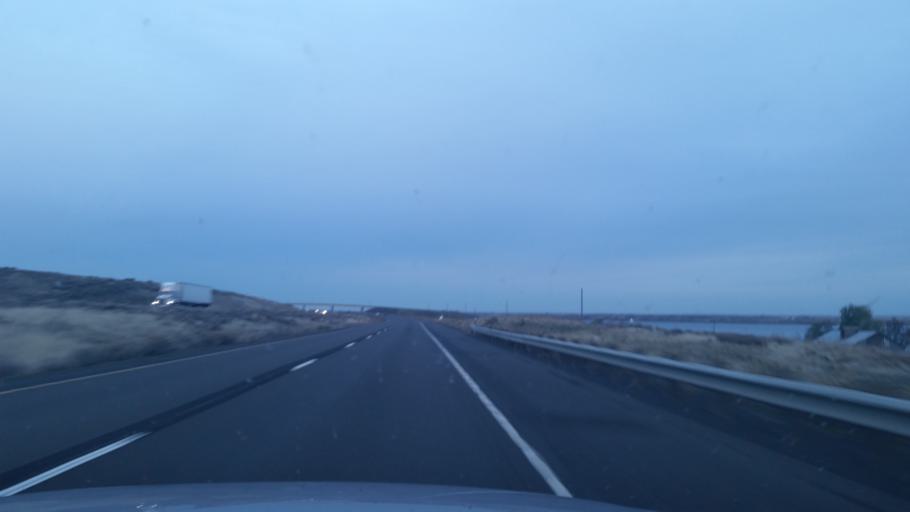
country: US
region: Washington
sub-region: Adams County
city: Ritzville
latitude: 47.2554
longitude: -118.0890
